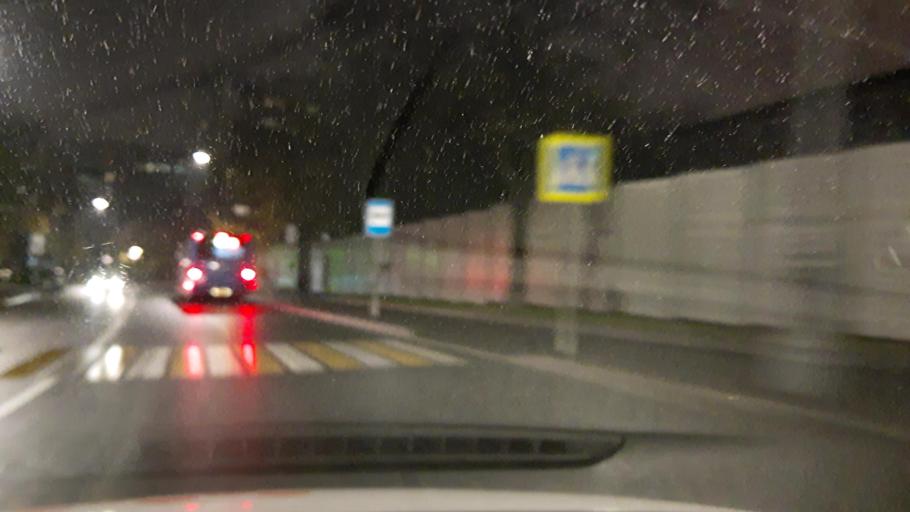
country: RU
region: Moskovskaya
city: Alekseyevka
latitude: 55.6335
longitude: 37.8033
